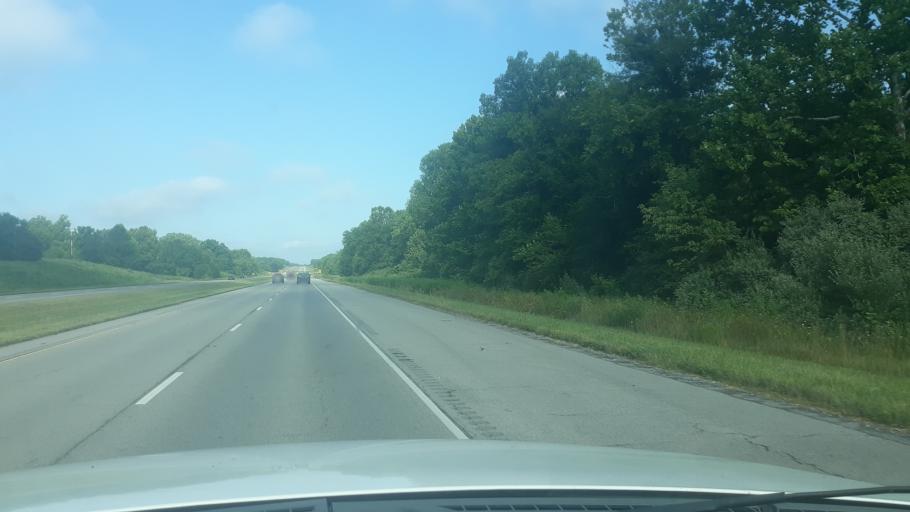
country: US
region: Illinois
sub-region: Saline County
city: Carrier Mills
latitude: 37.7308
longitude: -88.7461
